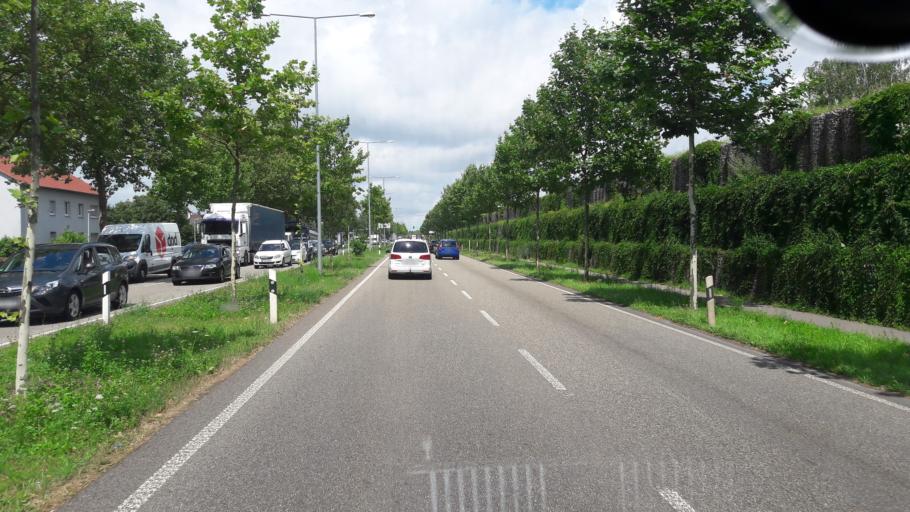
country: DE
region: Baden-Wuerttemberg
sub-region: Karlsruhe Region
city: Karlsruhe
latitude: 49.0261
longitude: 8.3578
